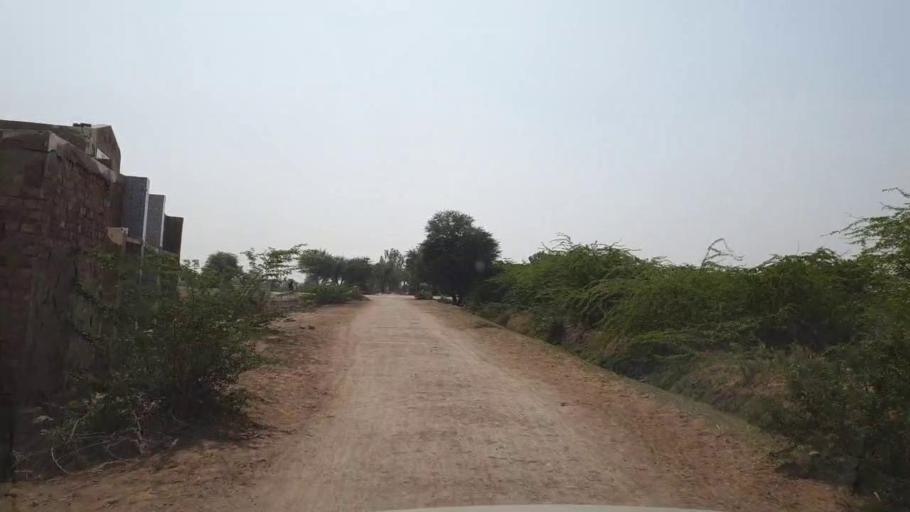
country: PK
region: Sindh
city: Dhoro Naro
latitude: 25.4770
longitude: 69.6396
